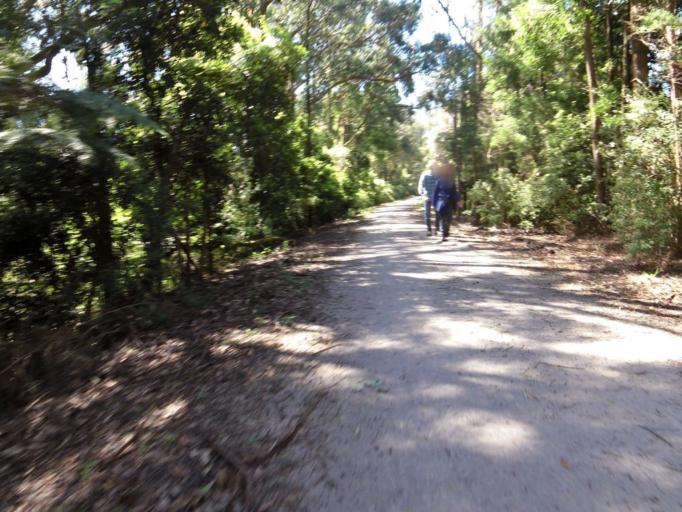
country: AU
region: Victoria
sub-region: Latrobe
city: Morwell
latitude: -38.6699
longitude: 146.1719
